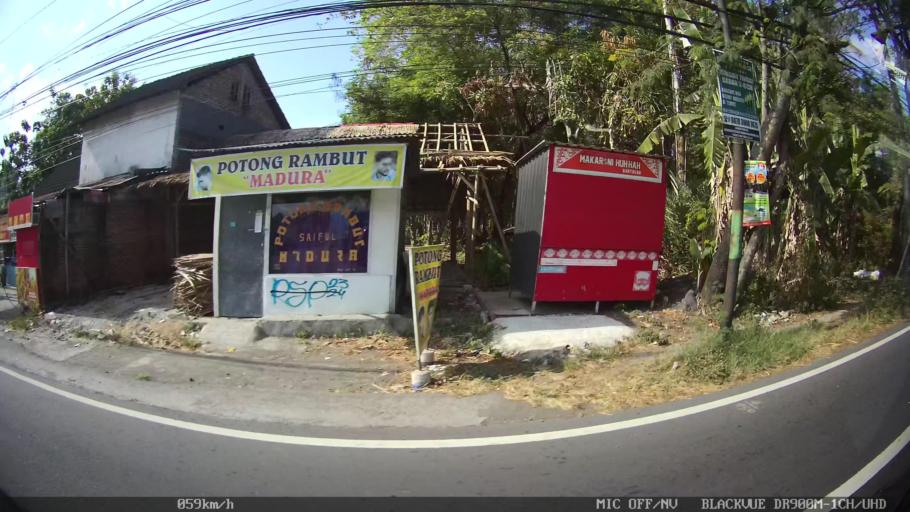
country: ID
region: Daerah Istimewa Yogyakarta
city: Gamping Lor
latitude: -7.8075
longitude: 110.2914
